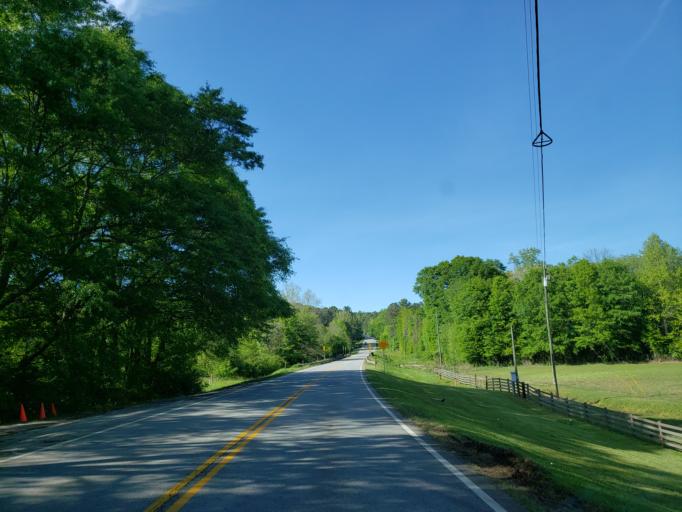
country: US
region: Georgia
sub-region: Haralson County
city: Tallapoosa
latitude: 33.7056
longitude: -85.2715
